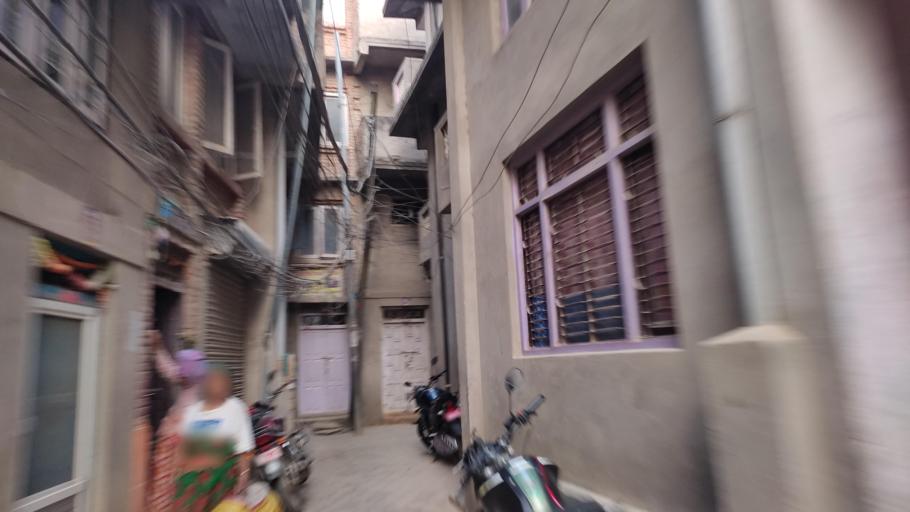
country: NP
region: Central Region
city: Kirtipur
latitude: 27.6713
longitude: 85.2850
